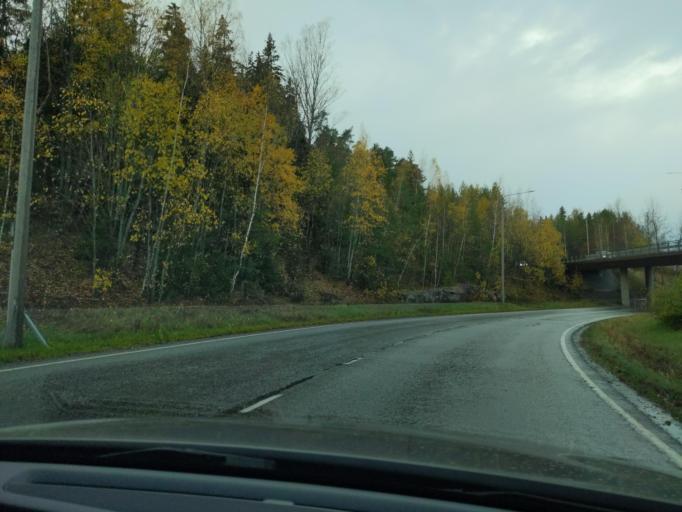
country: FI
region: Varsinais-Suomi
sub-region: Turku
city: Raisio
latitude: 60.4656
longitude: 22.1332
